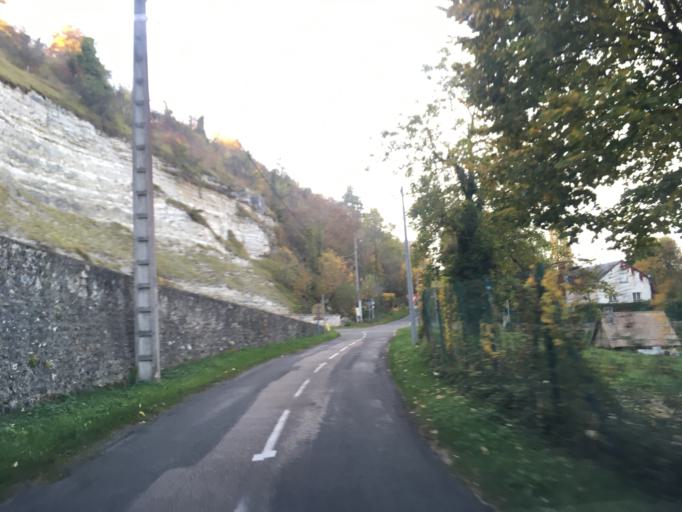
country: FR
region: Haute-Normandie
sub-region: Departement de l'Eure
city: Heudreville-sur-Eure
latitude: 49.1140
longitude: 1.2080
